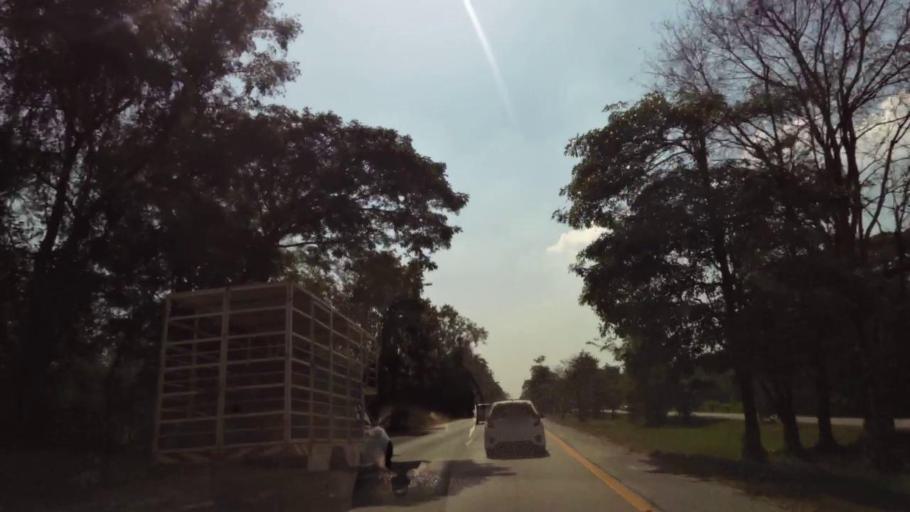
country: TH
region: Phichit
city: Wachira Barami
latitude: 16.5541
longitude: 100.1471
